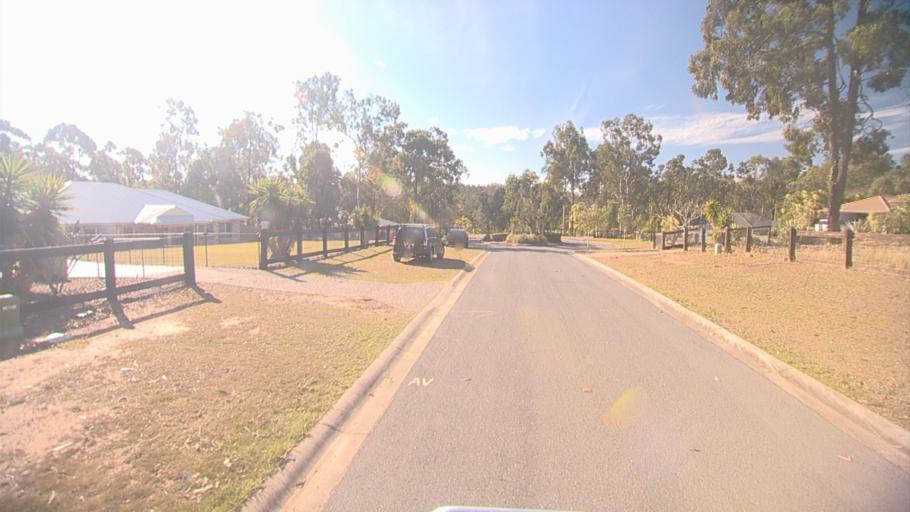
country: AU
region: Queensland
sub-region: Ipswich
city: Springfield Lakes
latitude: -27.7171
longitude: 152.9206
